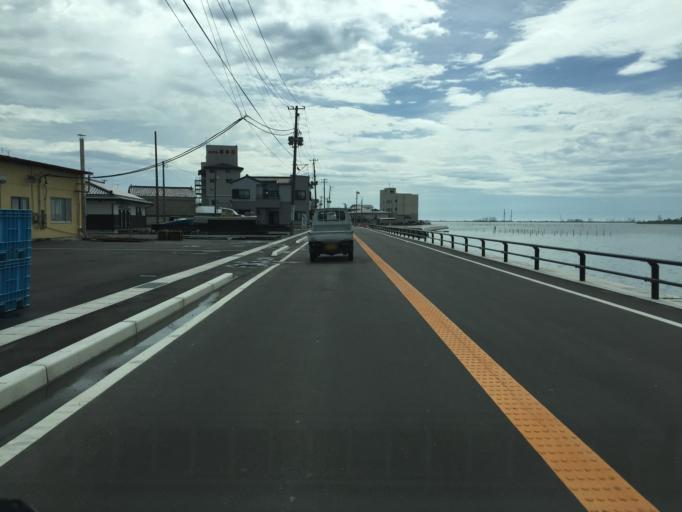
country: JP
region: Miyagi
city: Marumori
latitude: 37.8229
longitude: 140.9616
